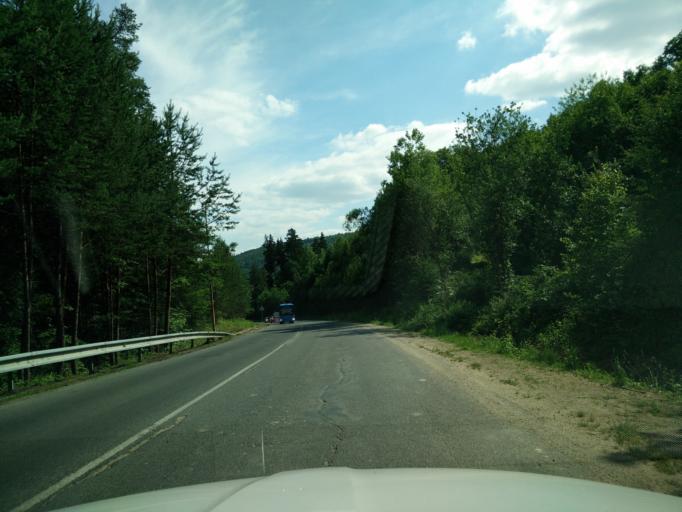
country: SK
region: Nitriansky
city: Bojnice
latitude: 48.8084
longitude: 18.5786
